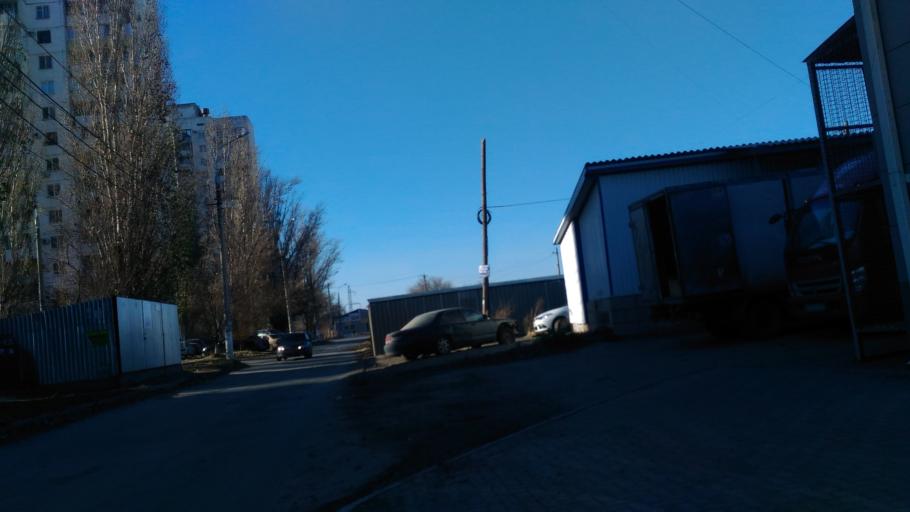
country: RU
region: Volgograd
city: Volgograd
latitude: 48.6556
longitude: 44.4346
